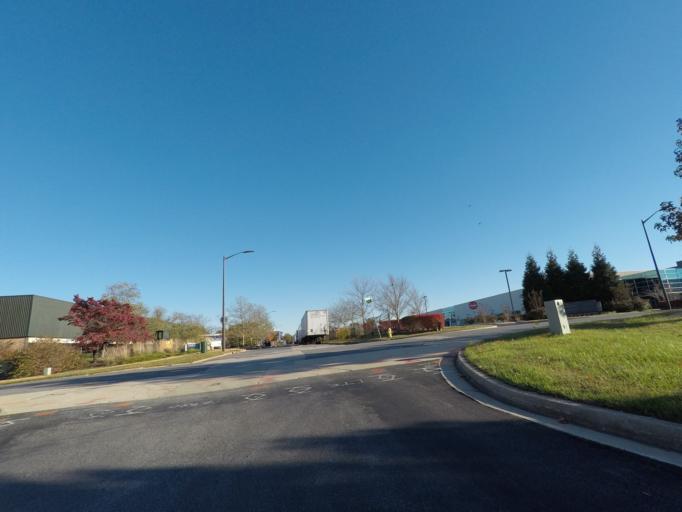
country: US
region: Maryland
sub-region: Howard County
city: Hanover
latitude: 39.1765
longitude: -76.7312
